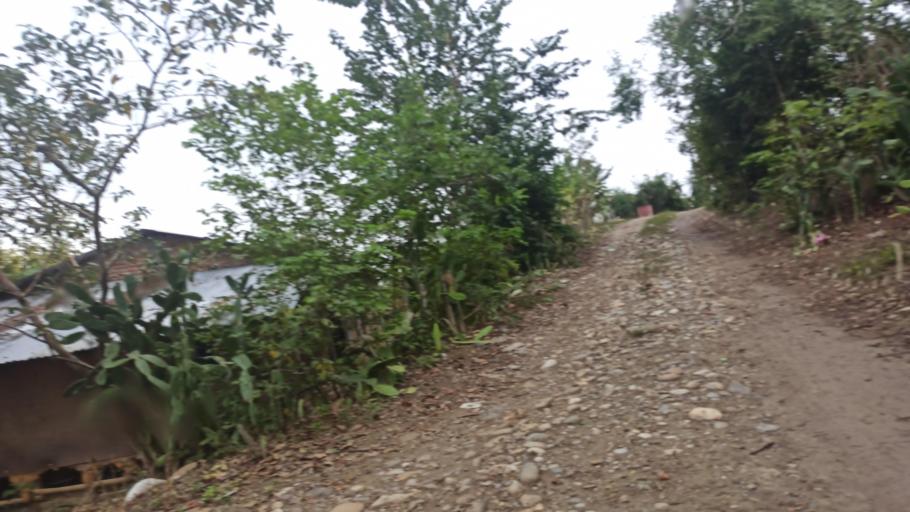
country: MX
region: Veracruz
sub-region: Papantla
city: El Chote
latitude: 20.3856
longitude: -97.3542
